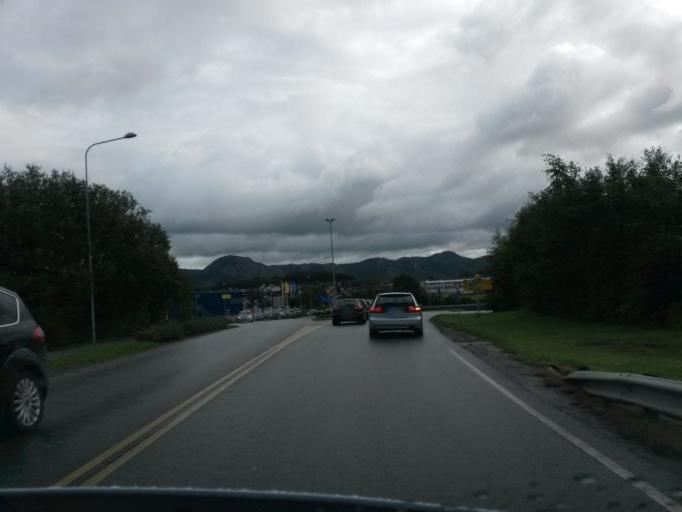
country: NO
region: Rogaland
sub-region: Sandnes
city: Sandnes
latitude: 58.8865
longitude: 5.7184
